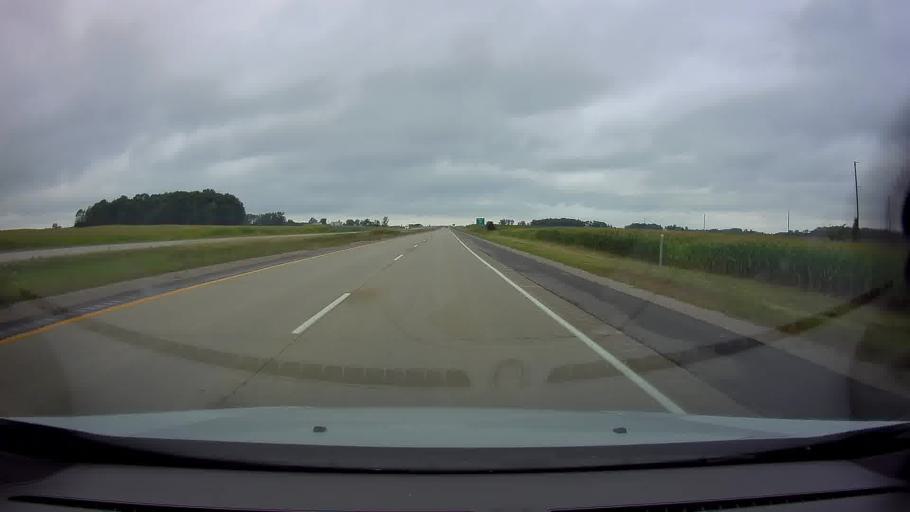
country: US
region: Wisconsin
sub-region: Brown County
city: Pulaski
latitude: 44.6586
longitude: -88.3025
